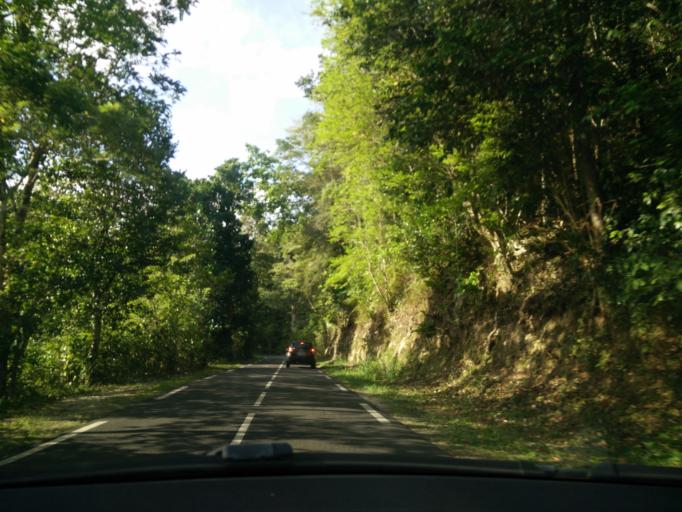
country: GP
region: Guadeloupe
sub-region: Guadeloupe
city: Sainte-Anne
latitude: 16.2676
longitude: -61.4215
